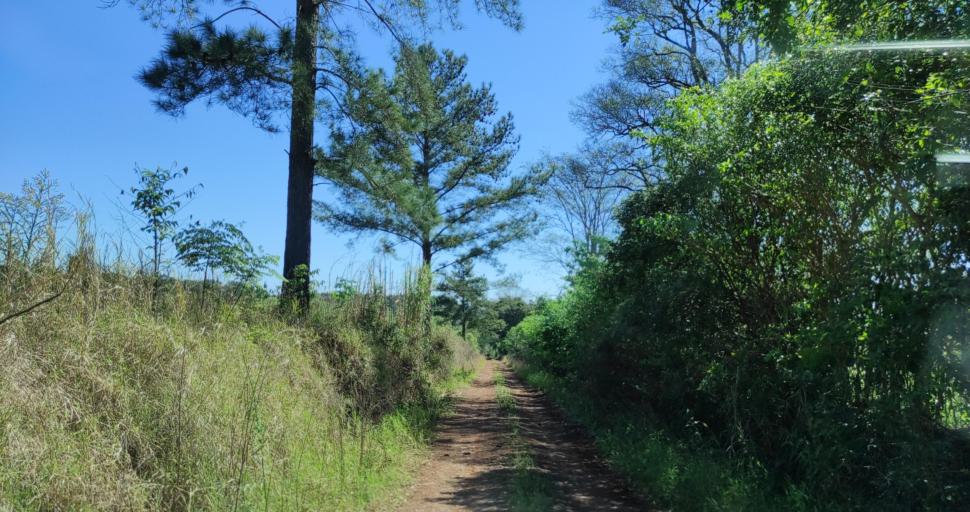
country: AR
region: Misiones
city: Ruiz de Montoya
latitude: -26.9526
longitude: -54.9941
